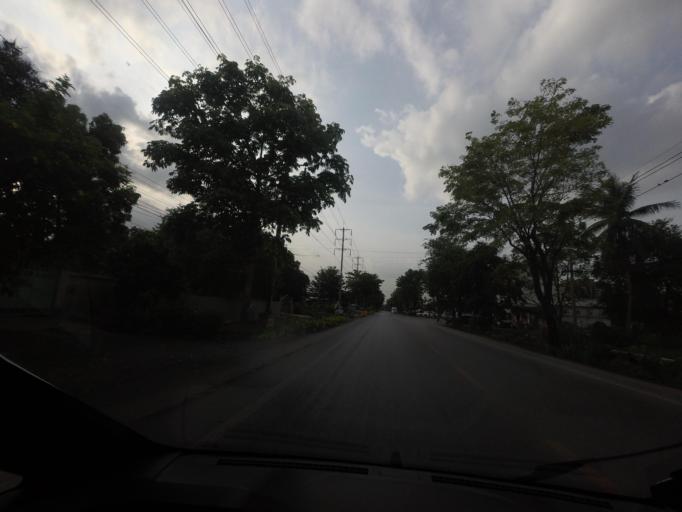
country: TH
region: Bangkok
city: Nong Chok
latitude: 13.8925
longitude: 100.8634
